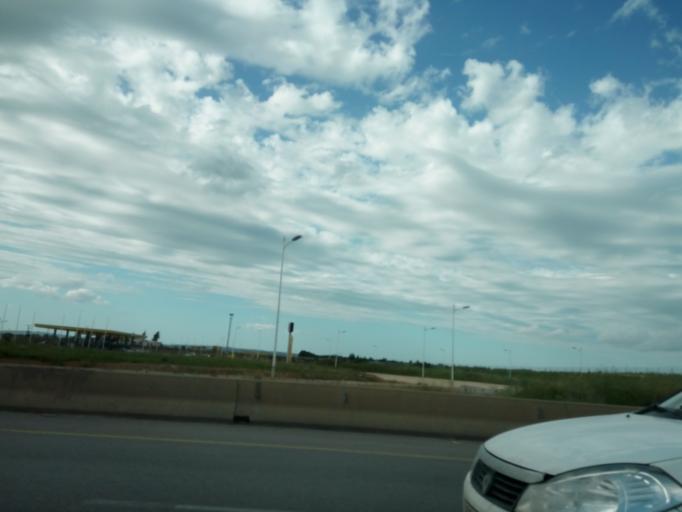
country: DZ
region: Tipaza
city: Mouzaia
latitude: 36.4494
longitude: 2.6605
